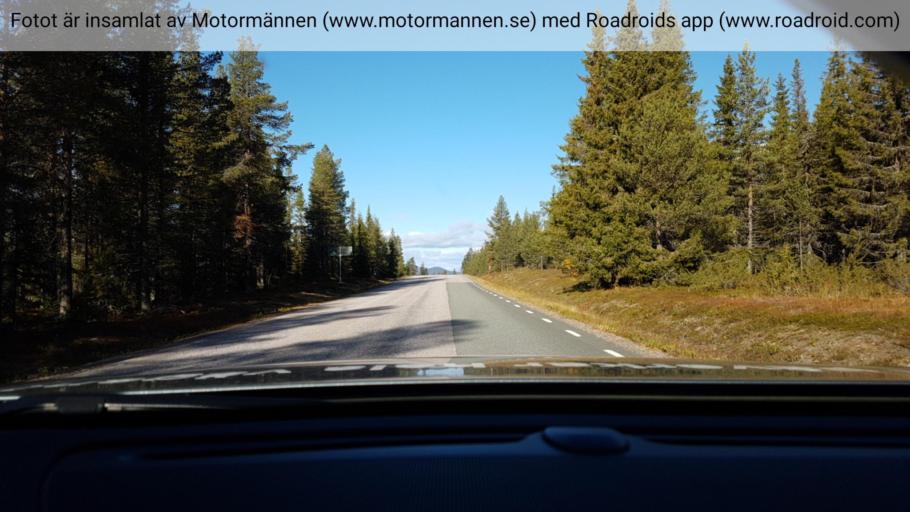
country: SE
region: Norrbotten
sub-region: Arjeplogs Kommun
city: Arjeplog
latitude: 65.7897
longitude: 18.4868
